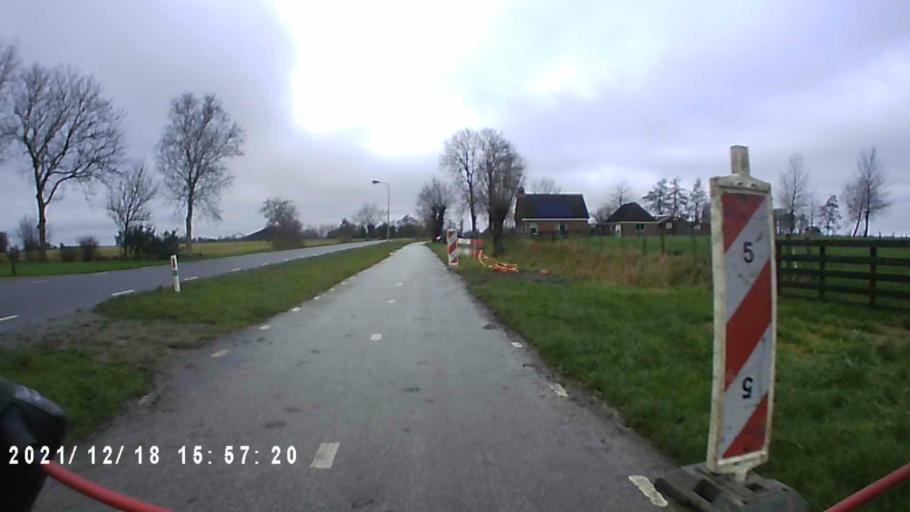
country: NL
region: Friesland
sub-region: Gemeente Dongeradeel
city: Anjum
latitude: 53.3343
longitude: 6.0957
